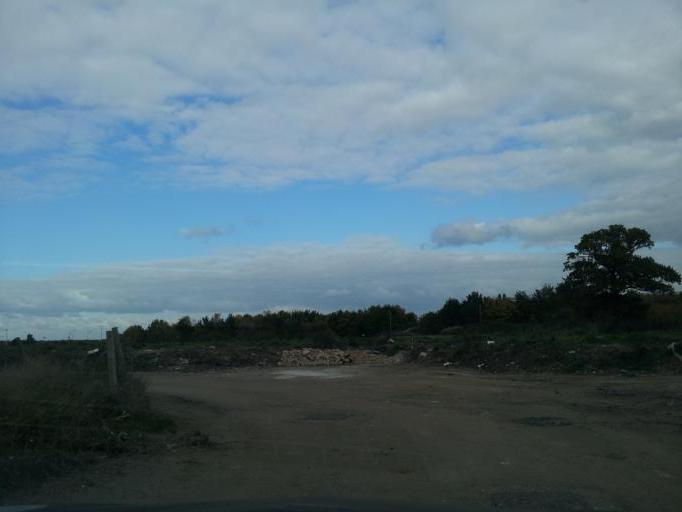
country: GB
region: England
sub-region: Milton Keynes
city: Shenley Church End
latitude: 51.9951
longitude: -0.7982
